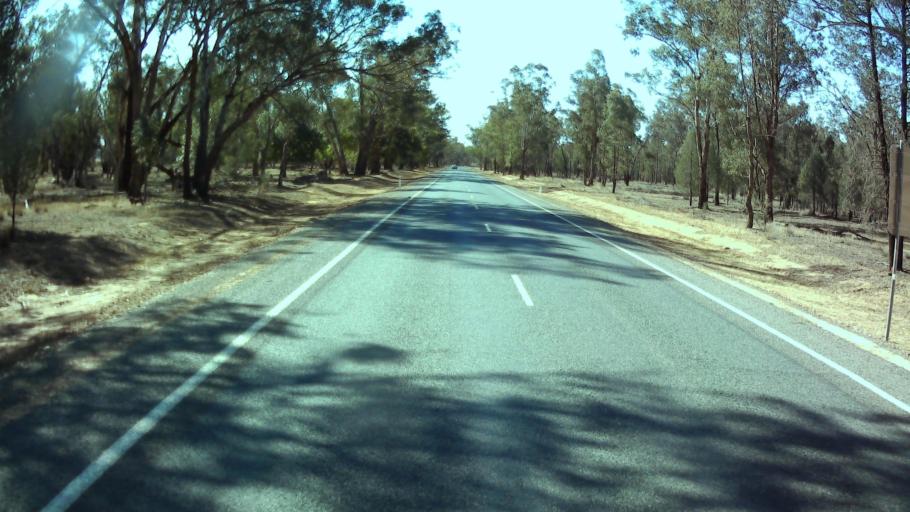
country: AU
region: New South Wales
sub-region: Weddin
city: Grenfell
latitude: -33.7246
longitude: 148.0851
